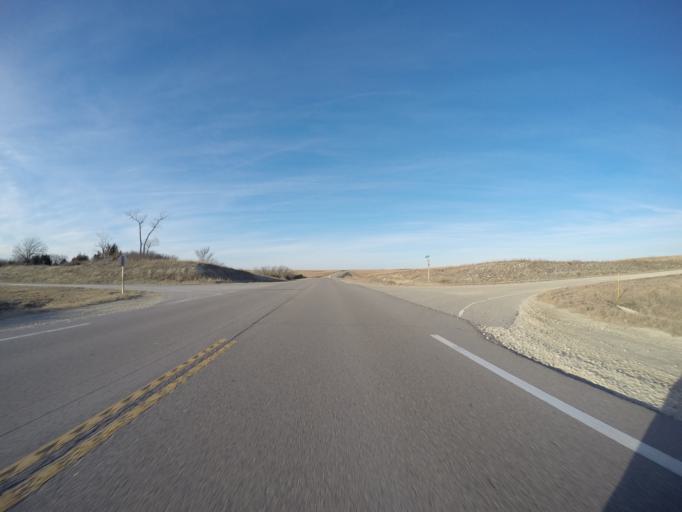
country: US
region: Kansas
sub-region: Marion County
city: Marion
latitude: 38.2900
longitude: -96.9652
